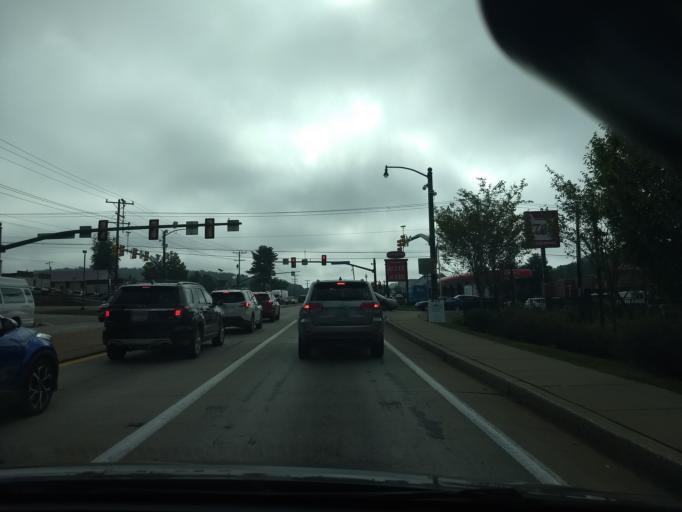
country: US
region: Pennsylvania
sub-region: Westmoreland County
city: Murrysville
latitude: 40.4244
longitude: -79.6675
